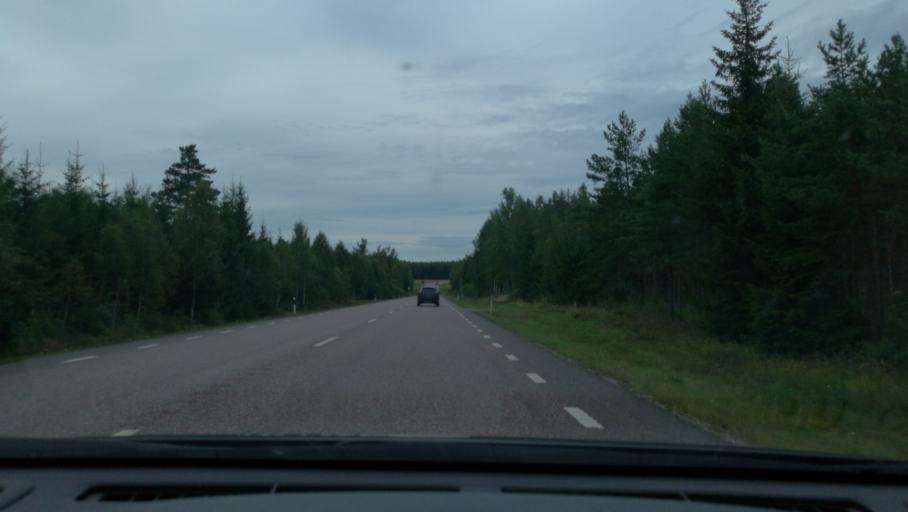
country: SE
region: Soedermanland
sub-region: Katrineholms Kommun
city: Katrineholm
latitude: 59.0501
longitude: 16.2212
